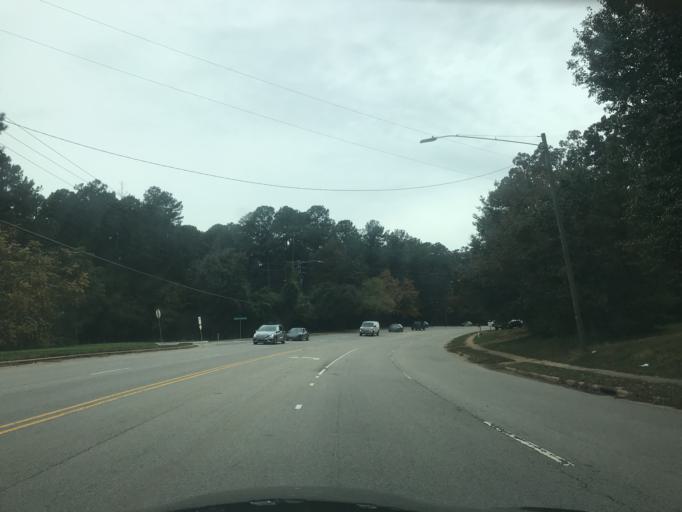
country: US
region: North Carolina
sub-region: Wake County
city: West Raleigh
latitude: 35.8567
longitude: -78.6761
